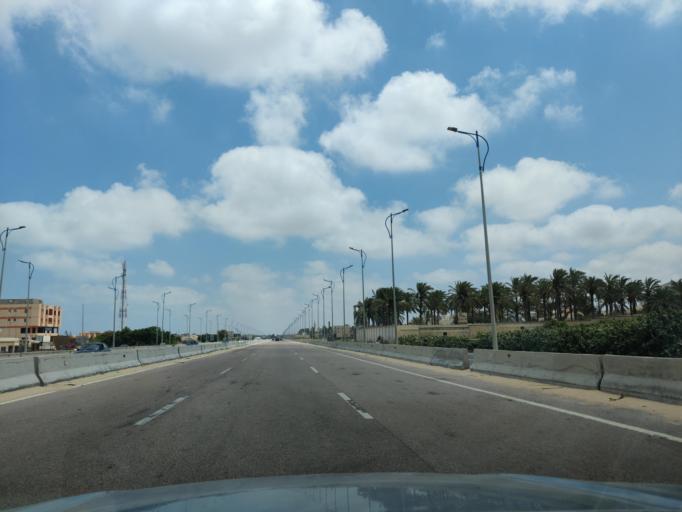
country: EG
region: Alexandria
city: Alexandria
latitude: 30.9805
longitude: 29.5778
